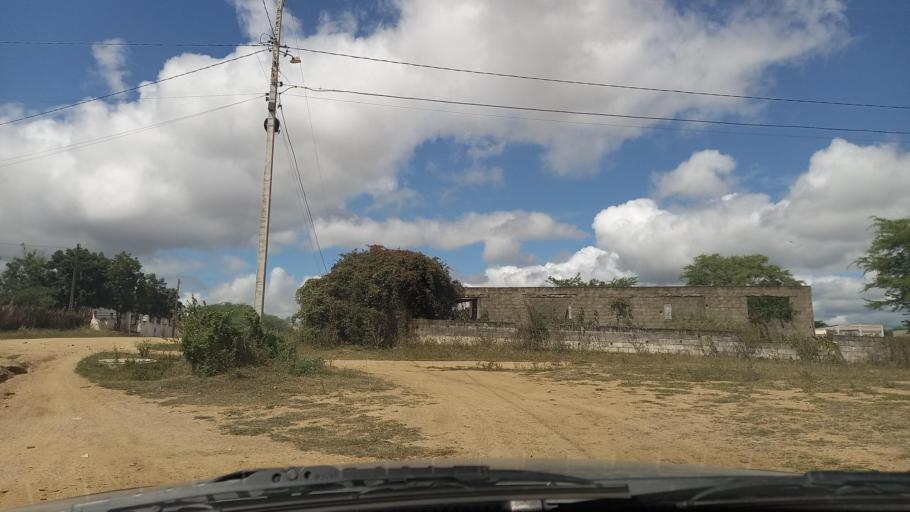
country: BR
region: Pernambuco
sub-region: Caruaru
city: Caruaru
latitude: -8.2529
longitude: -35.9814
